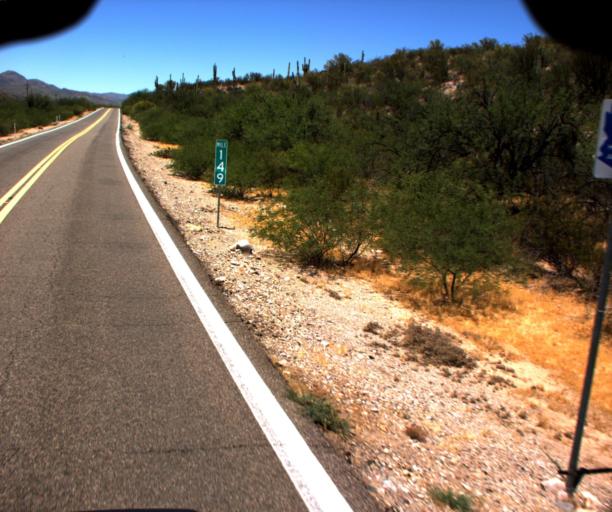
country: US
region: Arizona
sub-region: Pinal County
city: Kearny
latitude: 33.1023
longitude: -110.7456
